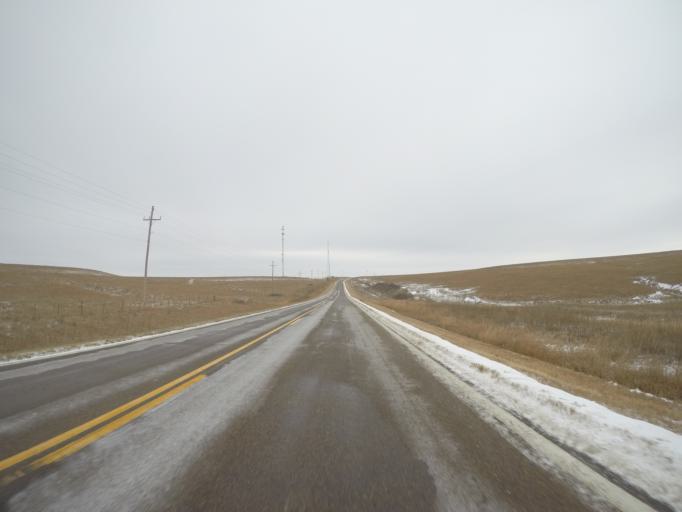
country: US
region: Kansas
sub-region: Wabaunsee County
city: Alma
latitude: 38.8700
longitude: -96.1424
